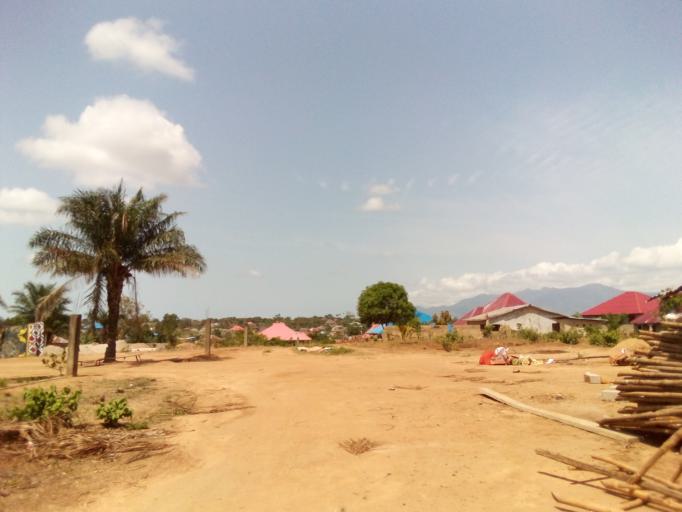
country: SL
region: Western Area
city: Waterloo
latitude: 8.3443
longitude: -13.0193
